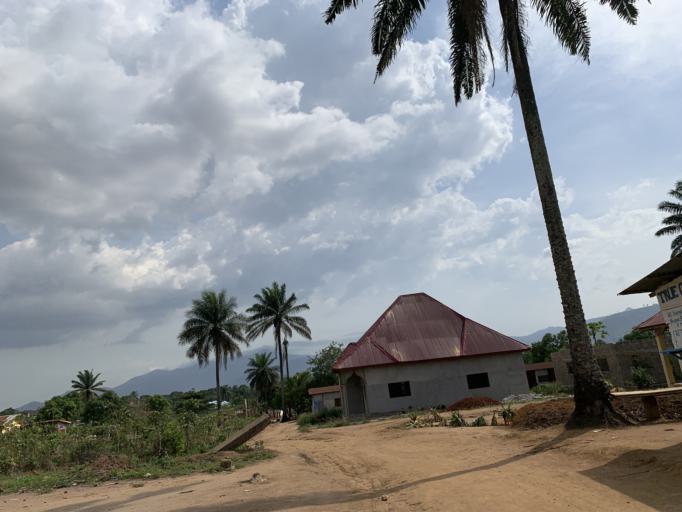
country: SL
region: Western Area
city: Waterloo
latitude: 8.3444
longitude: -13.0409
